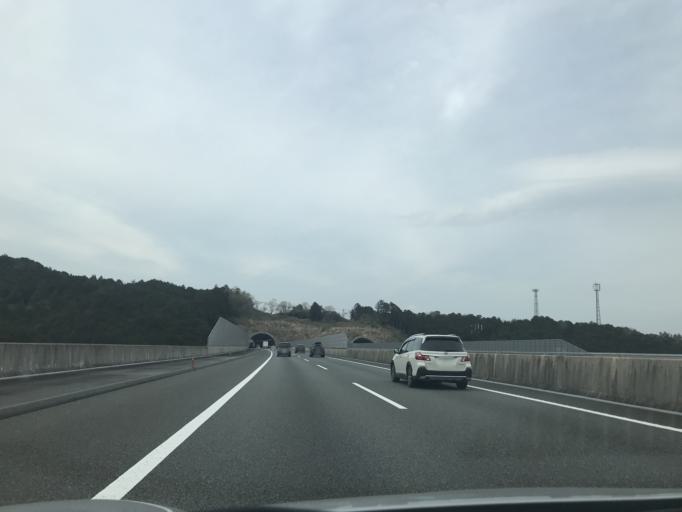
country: JP
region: Shizuoka
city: Mishima
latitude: 35.1918
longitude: 138.8890
